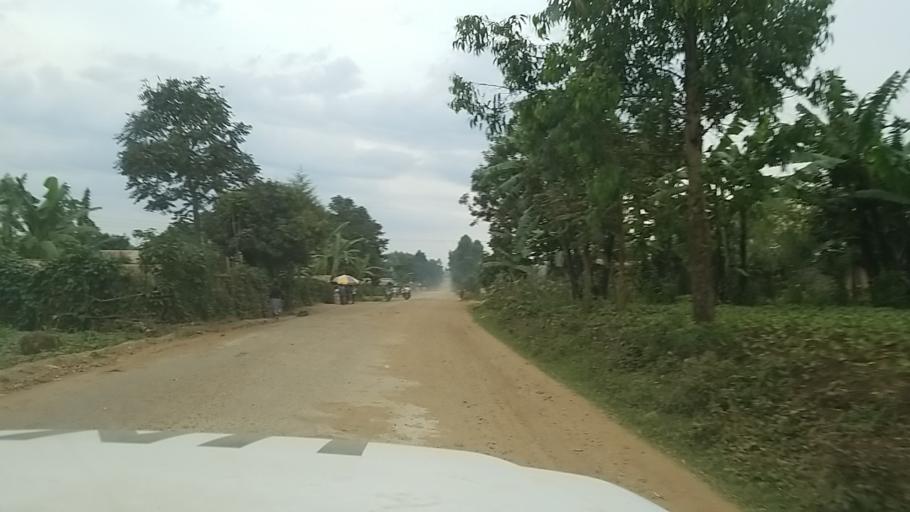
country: CD
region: South Kivu
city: Bukavu
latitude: -2.2683
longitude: 28.8196
